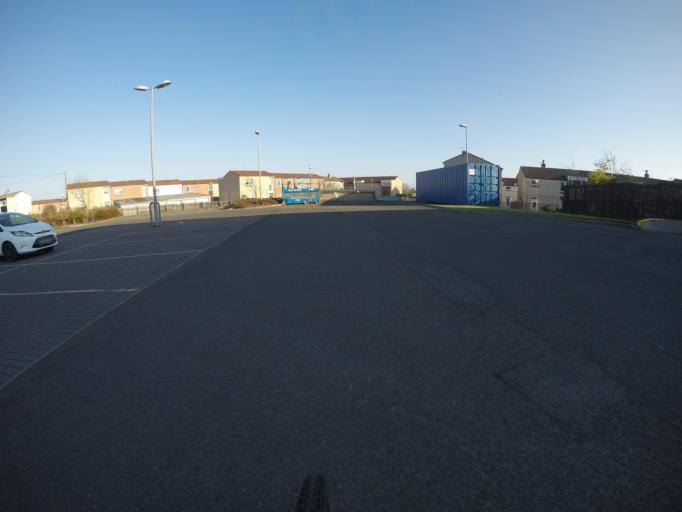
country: GB
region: Scotland
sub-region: North Ayrshire
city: Stevenston
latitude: 55.6386
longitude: -4.7613
